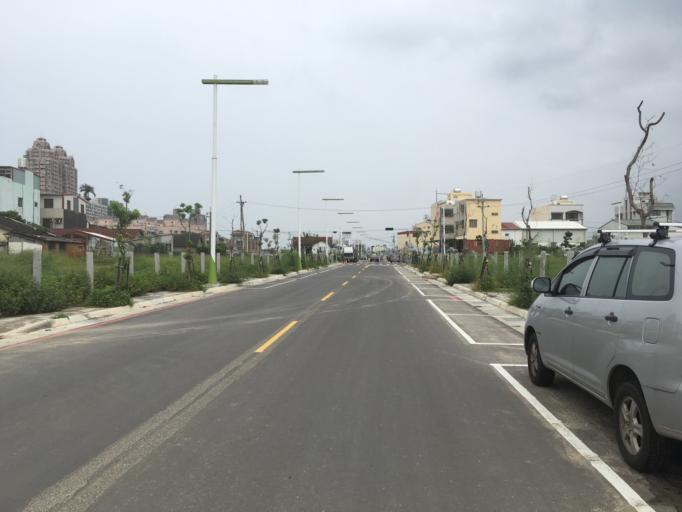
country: TW
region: Taiwan
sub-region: Taichung City
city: Taichung
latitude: 24.1842
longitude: 120.7043
